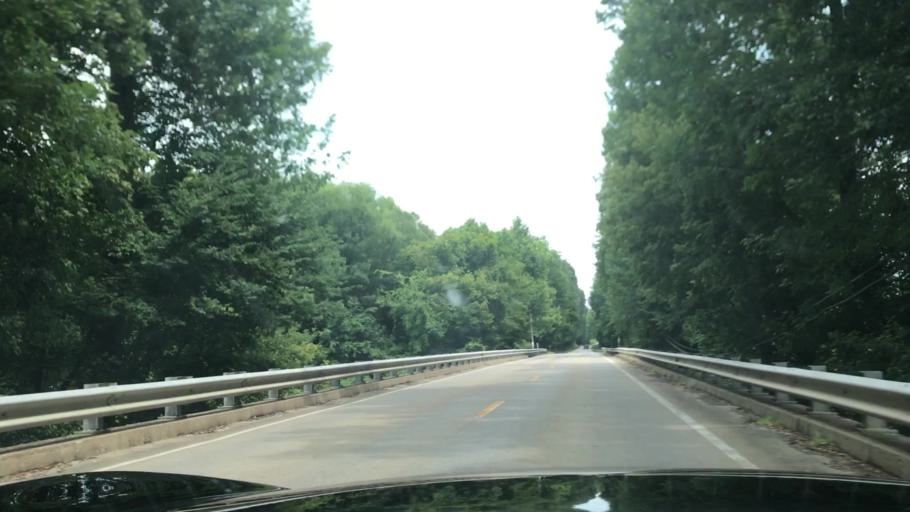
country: US
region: Kentucky
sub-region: Butler County
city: Morgantown
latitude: 37.1837
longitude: -86.7734
